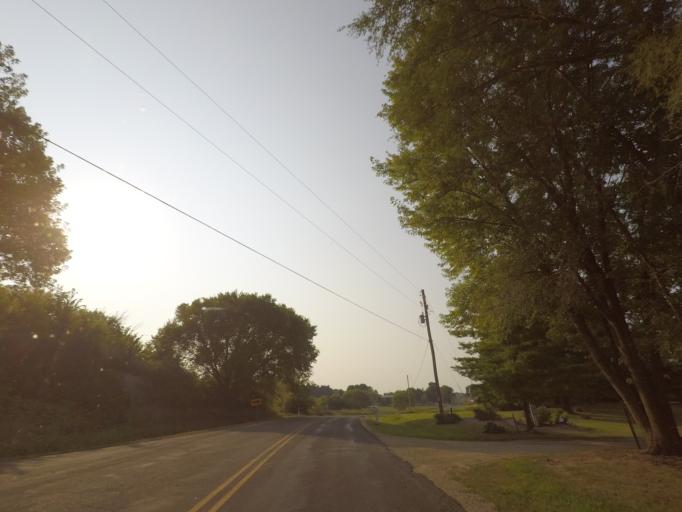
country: US
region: Wisconsin
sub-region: Dane County
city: Cottage Grove
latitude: 43.0423
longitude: -89.2299
